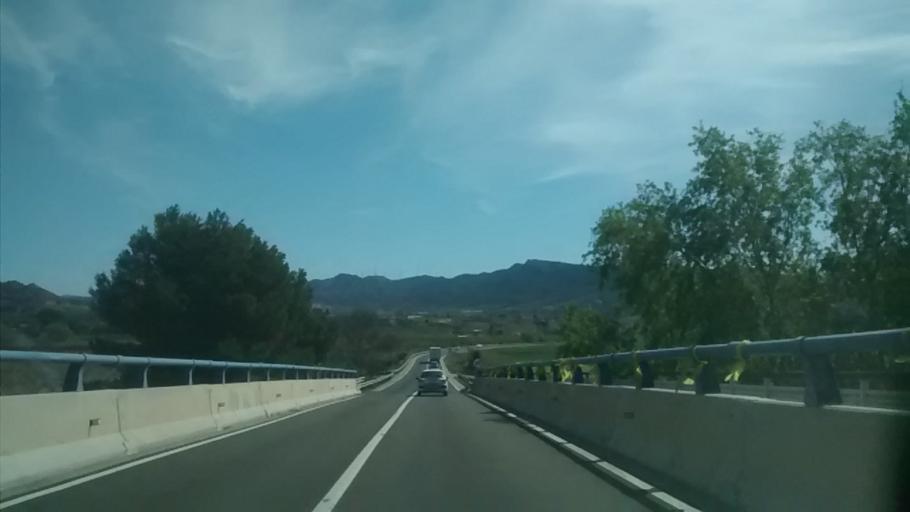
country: ES
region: Catalonia
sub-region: Provincia de Tarragona
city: Asco
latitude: 41.1874
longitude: 0.5711
